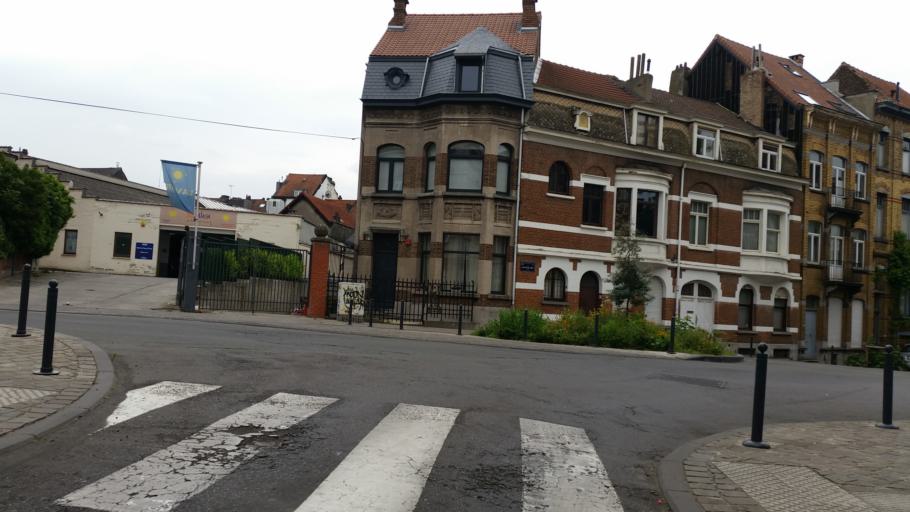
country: BE
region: Brussels Capital
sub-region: Bruxelles-Capitale
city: Brussels
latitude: 50.8726
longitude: 4.3838
